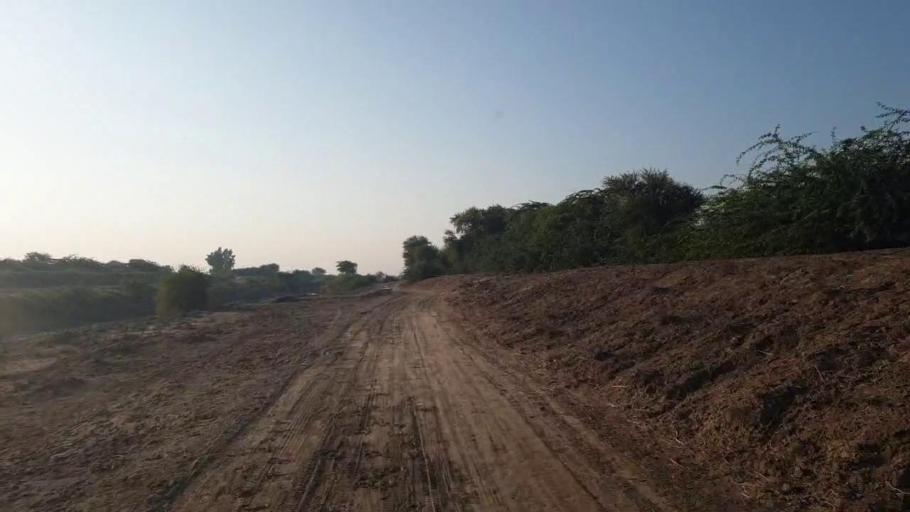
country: PK
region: Sindh
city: Badin
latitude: 24.6461
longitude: 68.7902
